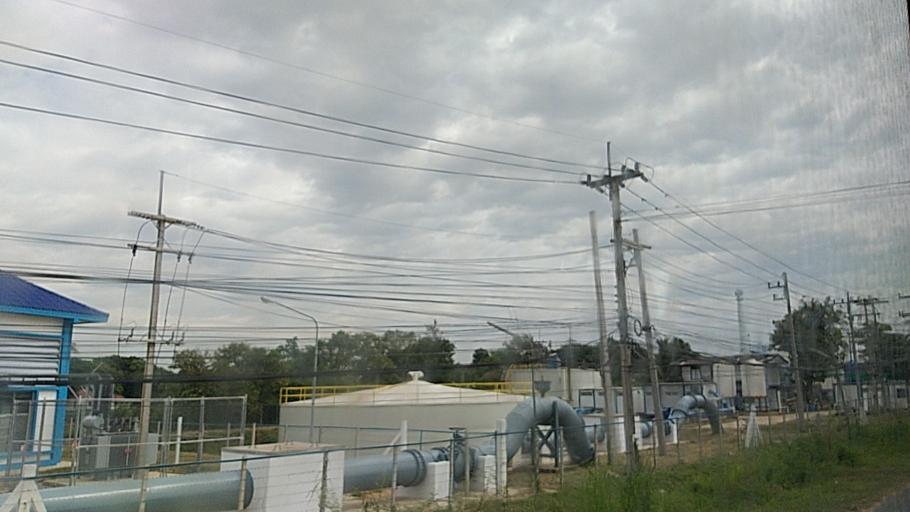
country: TH
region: Maha Sarakham
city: Maha Sarakham
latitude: 16.2172
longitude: 103.2769
